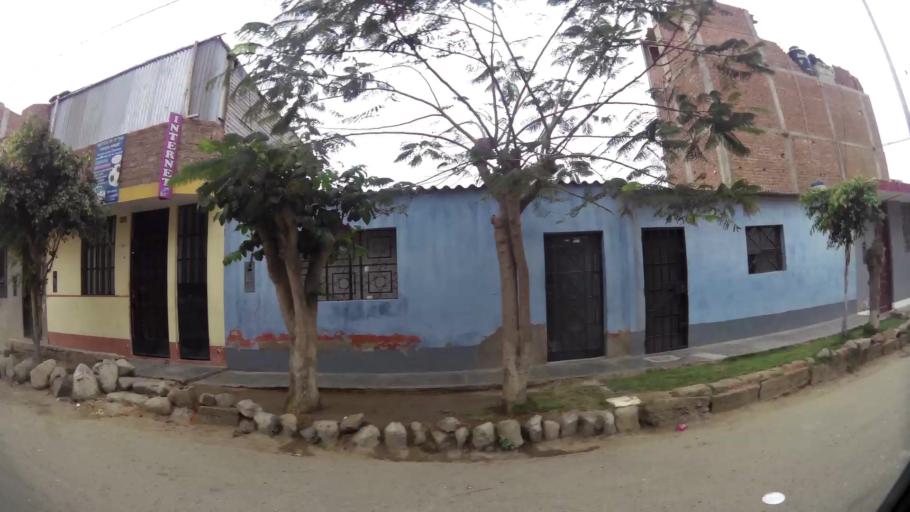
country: PE
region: La Libertad
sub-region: Provincia de Trujillo
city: La Esperanza
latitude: -8.0800
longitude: -79.0521
